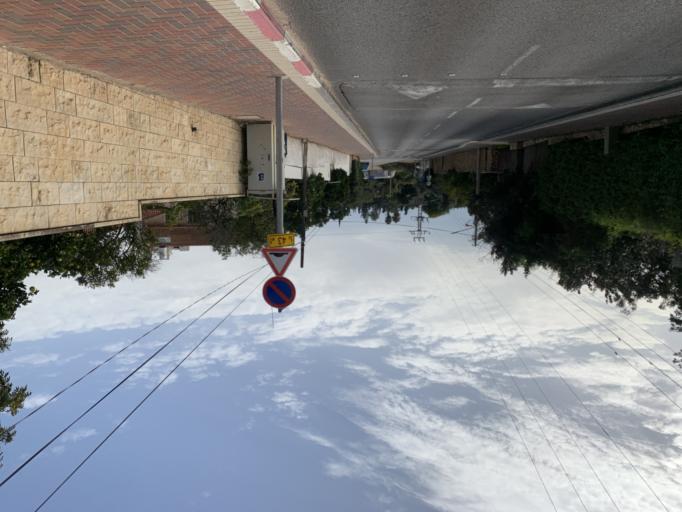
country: IL
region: Central District
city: Hod HaSharon
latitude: 32.1517
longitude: 34.8989
